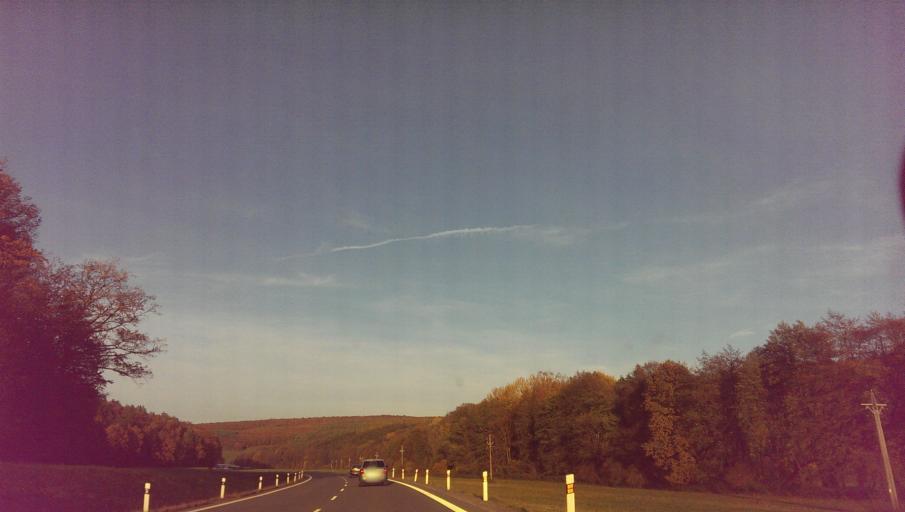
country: CZ
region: Zlin
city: Brezolupy
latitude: 49.1329
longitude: 17.5972
